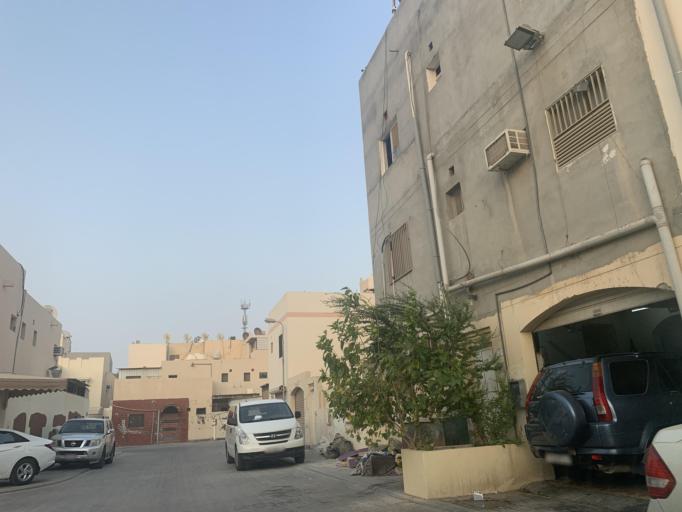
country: BH
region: Manama
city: Jidd Hafs
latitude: 26.2202
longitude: 50.5157
